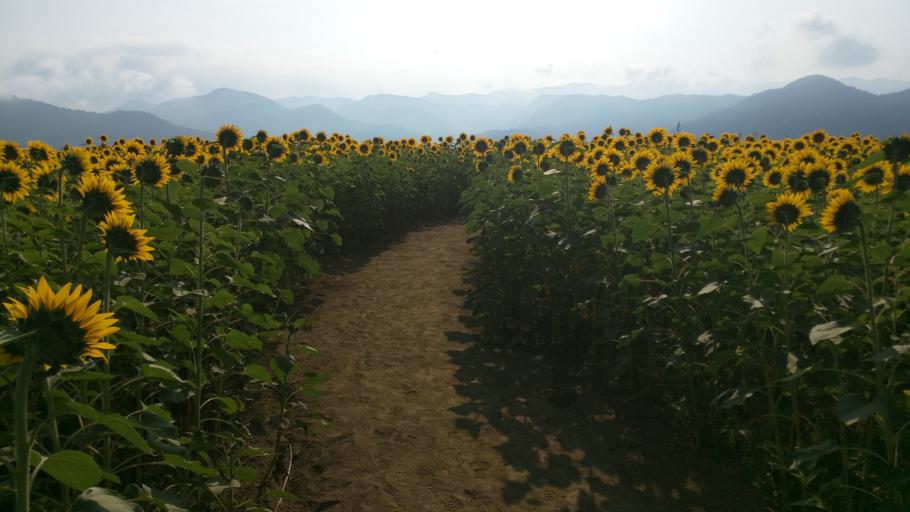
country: JP
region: Fukushima
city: Kitakata
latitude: 37.7486
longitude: 139.8660
